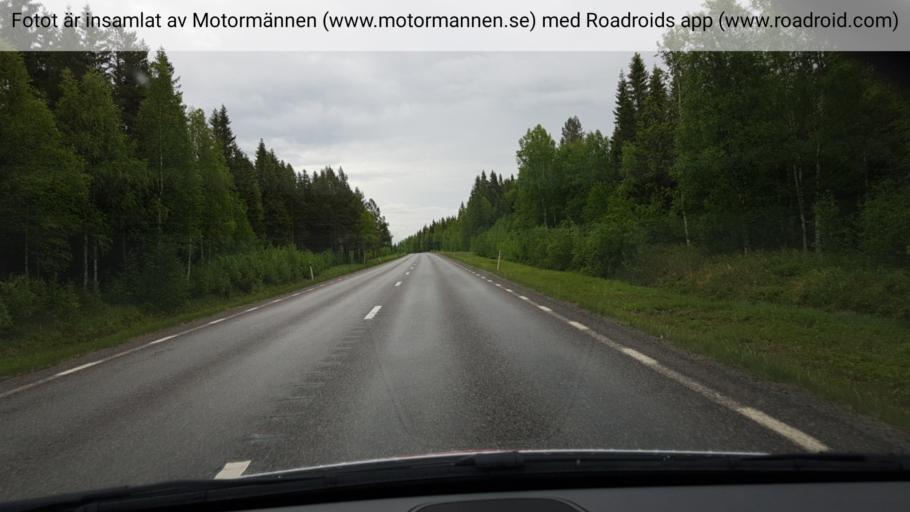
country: SE
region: Jaemtland
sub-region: OEstersunds Kommun
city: Brunflo
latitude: 63.1999
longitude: 14.9467
